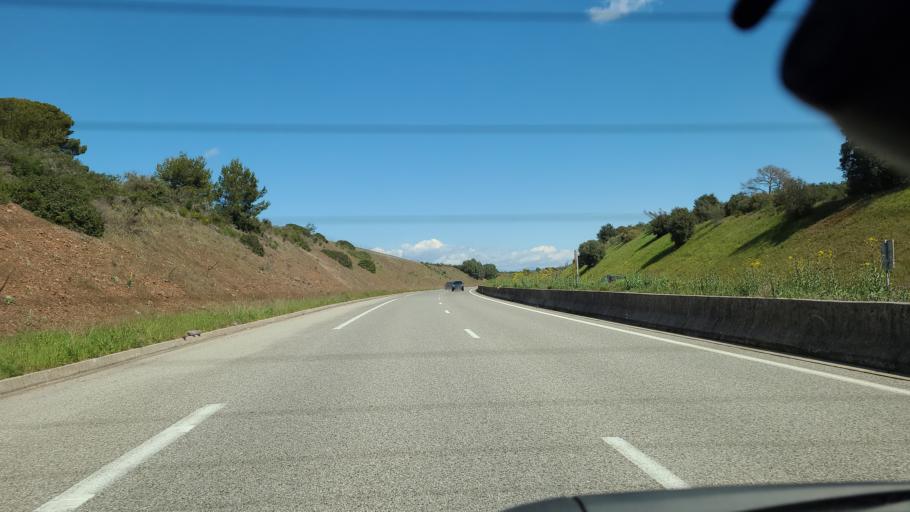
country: FR
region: Provence-Alpes-Cote d'Azur
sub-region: Departement du Var
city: Le Cannet-des-Maures
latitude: 43.3748
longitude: 6.3477
